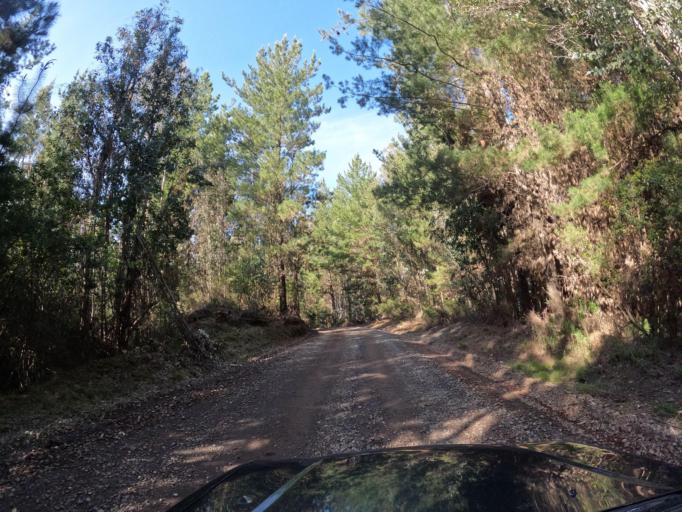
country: CL
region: Biobio
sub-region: Provincia de Biobio
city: La Laja
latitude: -37.0856
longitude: -72.7900
